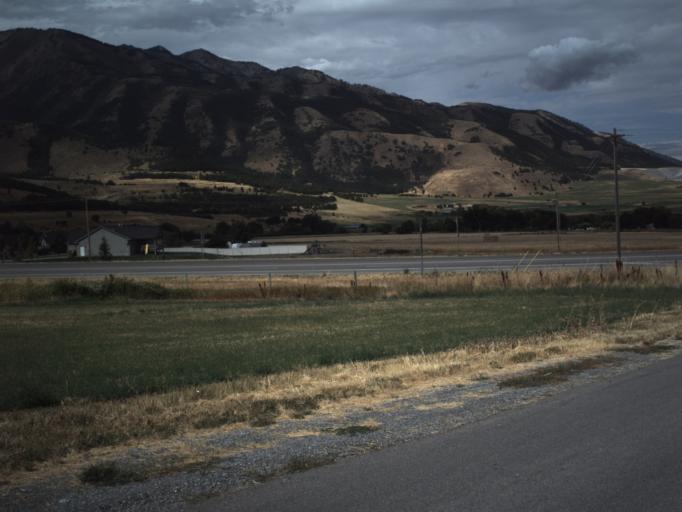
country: US
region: Utah
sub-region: Cache County
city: Wellsville
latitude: 41.6150
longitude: -111.9330
